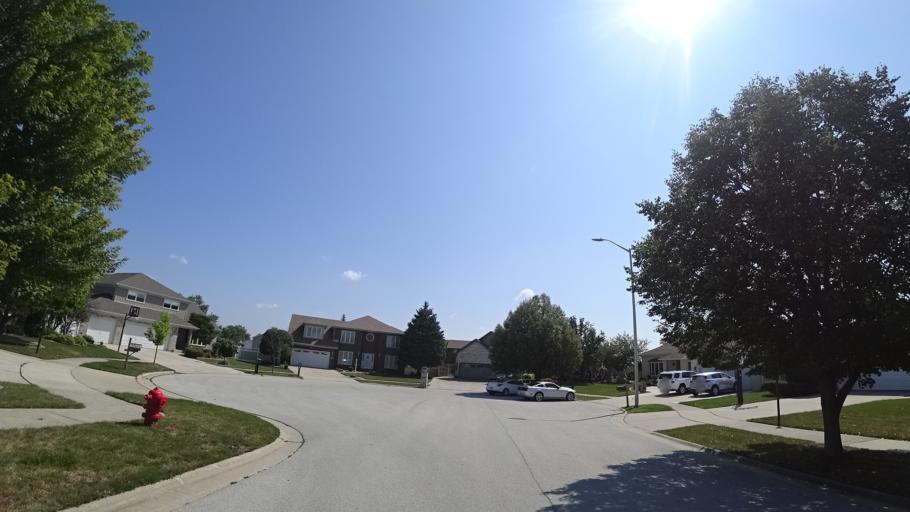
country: US
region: Illinois
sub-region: Cook County
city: Tinley Park
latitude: 41.6066
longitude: -87.7781
